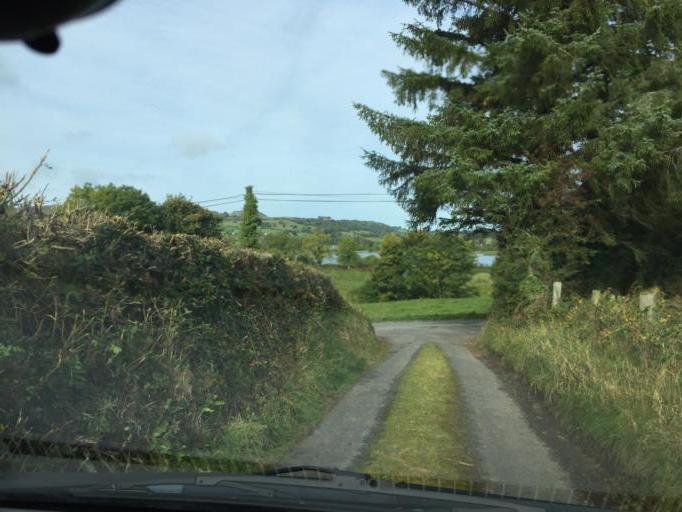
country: IE
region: Connaught
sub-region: Roscommon
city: Boyle
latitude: 54.0277
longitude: -8.3212
